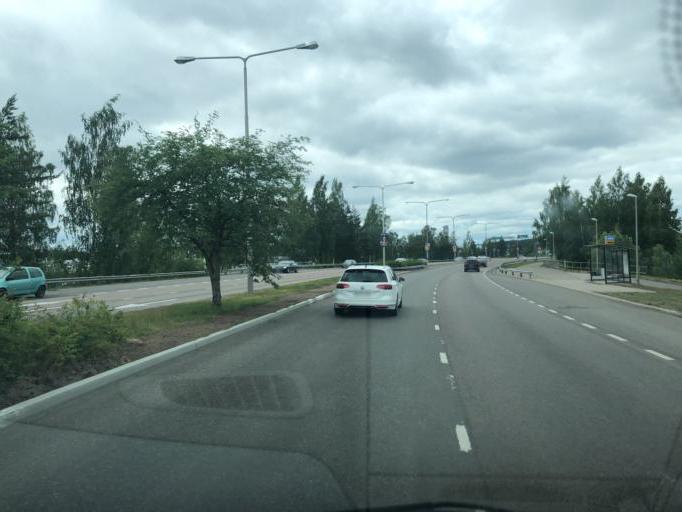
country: FI
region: Kymenlaakso
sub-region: Kouvola
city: Kouvola
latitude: 60.8717
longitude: 26.6615
